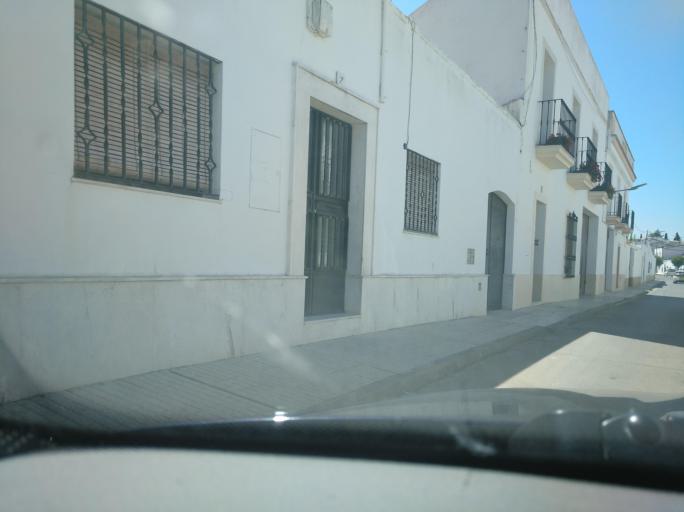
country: ES
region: Extremadura
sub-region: Provincia de Badajoz
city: Olivenza
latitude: 38.6811
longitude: -7.1016
